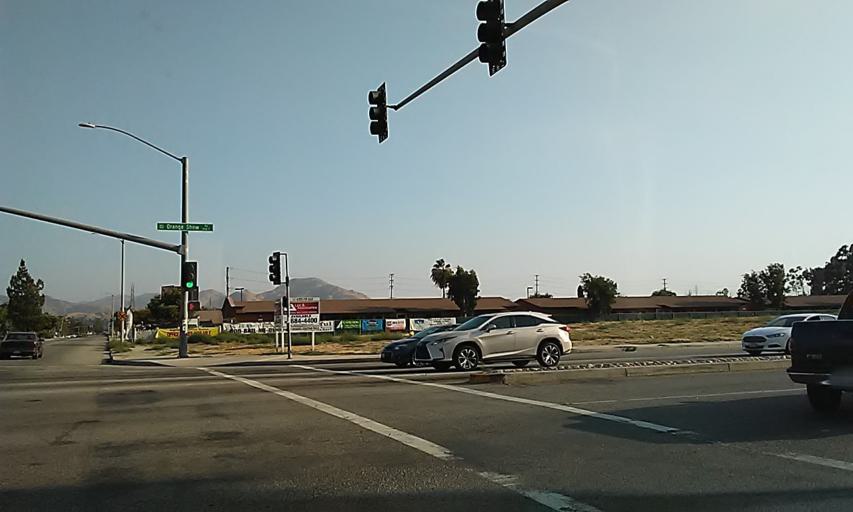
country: US
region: California
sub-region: San Bernardino County
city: San Bernardino
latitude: 34.0799
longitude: -117.2789
